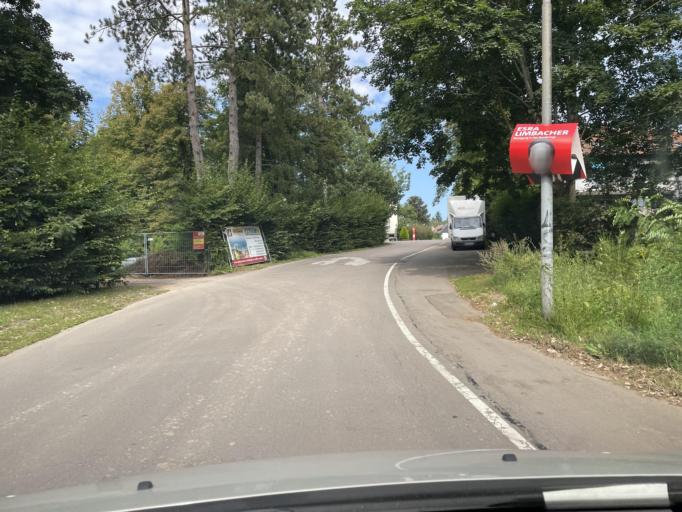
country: DE
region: Saarland
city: Sankt Ingbert
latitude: 49.2878
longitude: 7.1346
